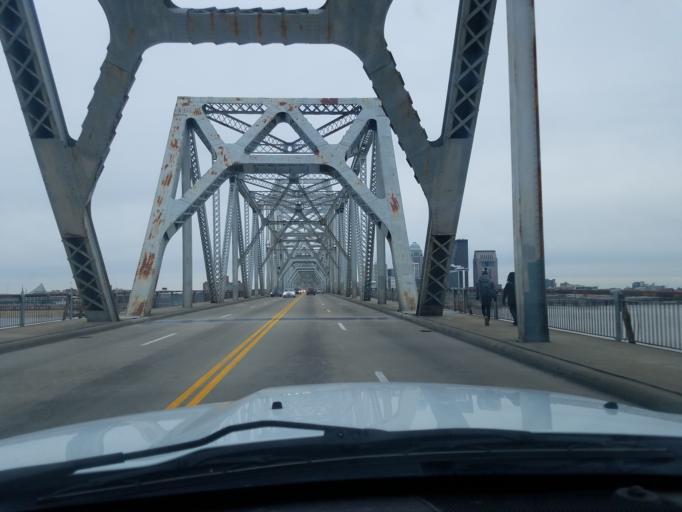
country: US
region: Kentucky
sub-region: Jefferson County
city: Louisville
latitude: 38.2678
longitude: -85.7507
